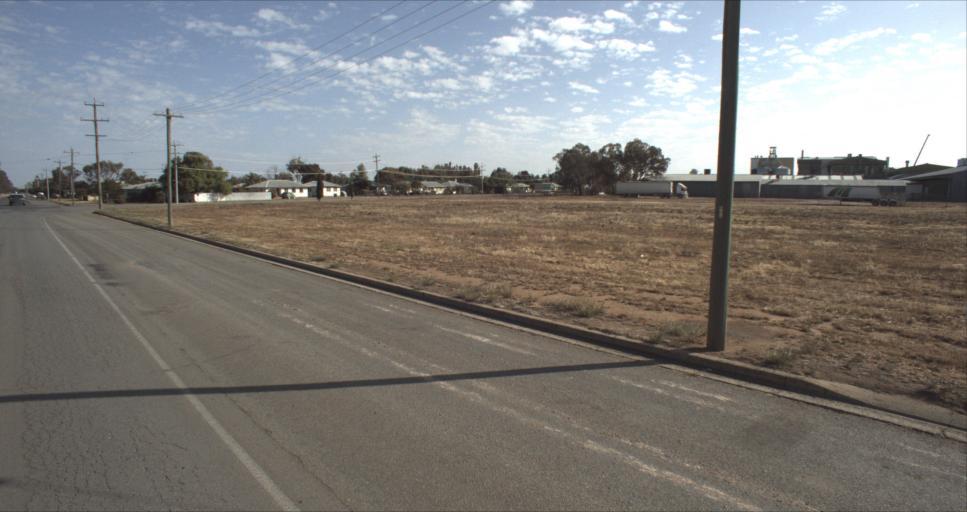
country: AU
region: New South Wales
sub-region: Leeton
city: Leeton
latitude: -34.5593
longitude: 146.3914
